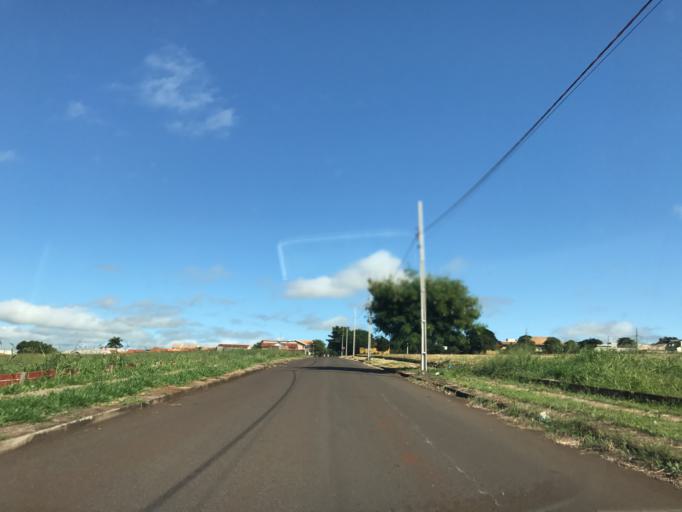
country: BR
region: Parana
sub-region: Maringa
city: Maringa
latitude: -23.4543
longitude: -51.9546
